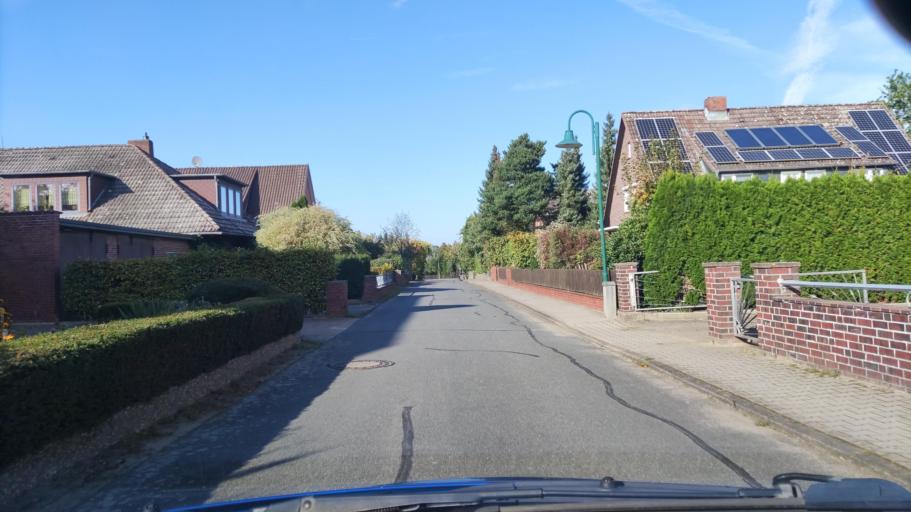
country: DE
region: Lower Saxony
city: Embsen
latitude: 53.1792
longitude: 10.3607
